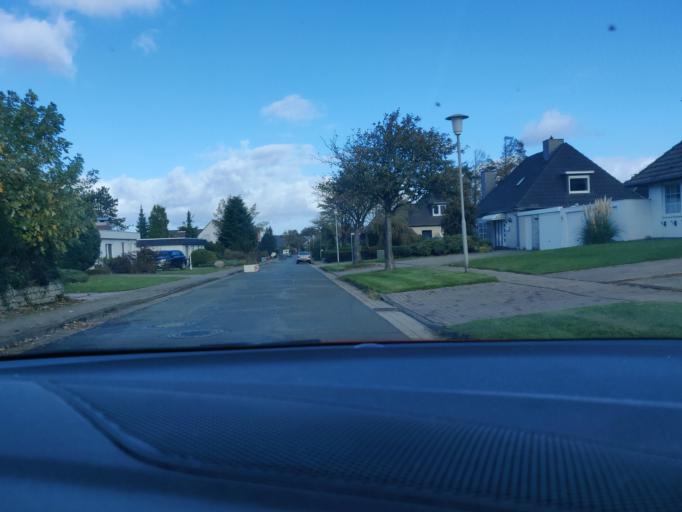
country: DE
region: Lower Saxony
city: Cuxhaven
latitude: 53.8707
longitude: 8.6477
